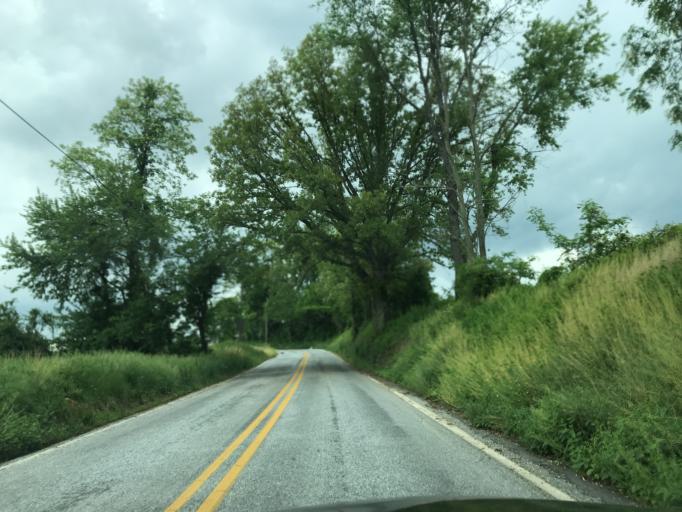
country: US
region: Pennsylvania
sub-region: York County
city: Susquehanna Trails
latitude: 39.7235
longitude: -76.3404
